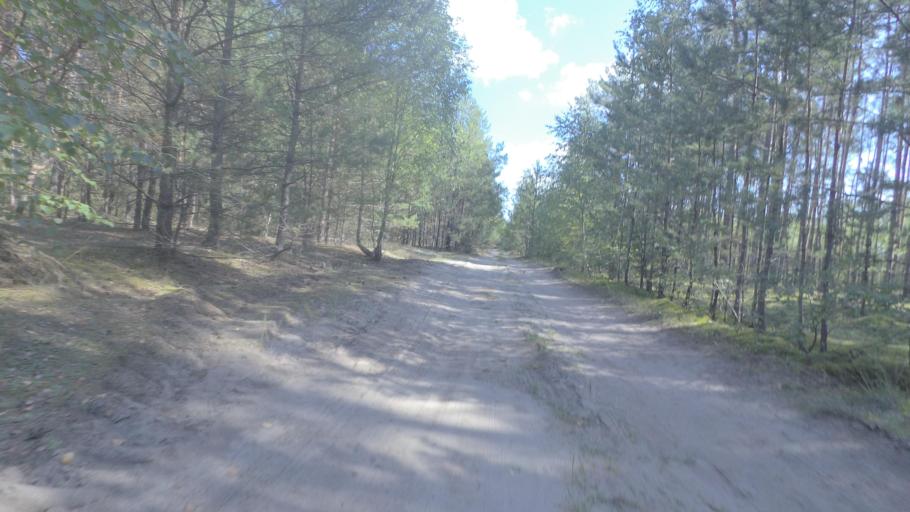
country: DE
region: Brandenburg
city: Halbe
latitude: 52.1510
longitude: 13.7219
